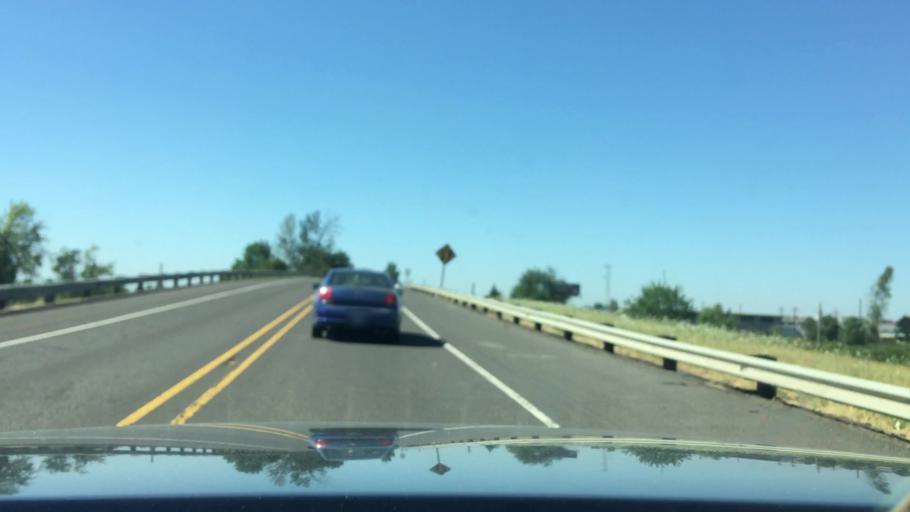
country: US
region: Oregon
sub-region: Lane County
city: Eugene
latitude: 44.0582
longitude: -123.1733
